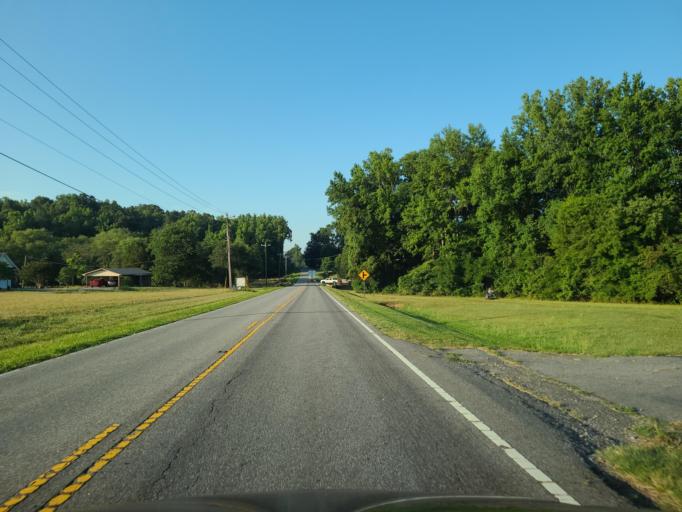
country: US
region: North Carolina
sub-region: Catawba County
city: Mountain View
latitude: 35.6543
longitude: -81.3807
